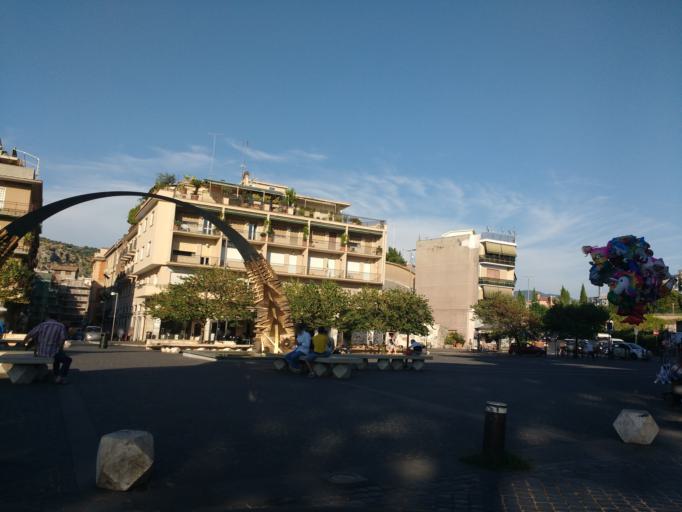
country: IT
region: Latium
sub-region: Citta metropolitana di Roma Capitale
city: Tivoli
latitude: 41.9613
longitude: 12.7963
